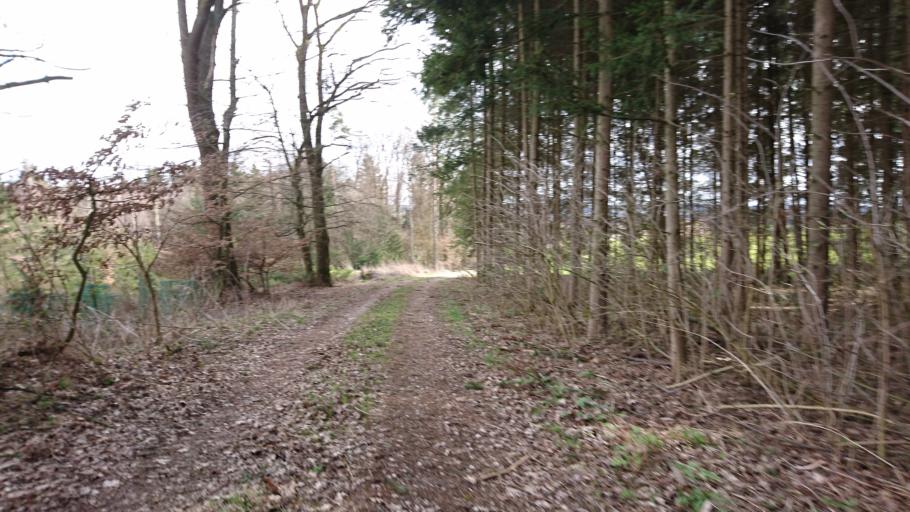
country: DE
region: Bavaria
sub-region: Swabia
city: Zusmarshausen
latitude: 48.4266
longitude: 10.5844
